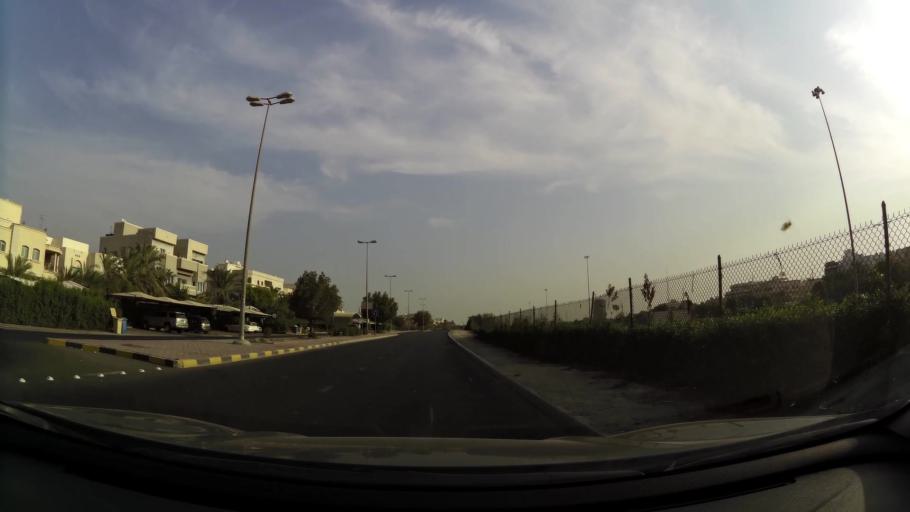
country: KW
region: Muhafazat Hawalli
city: Hawalli
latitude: 29.3145
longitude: 48.0194
